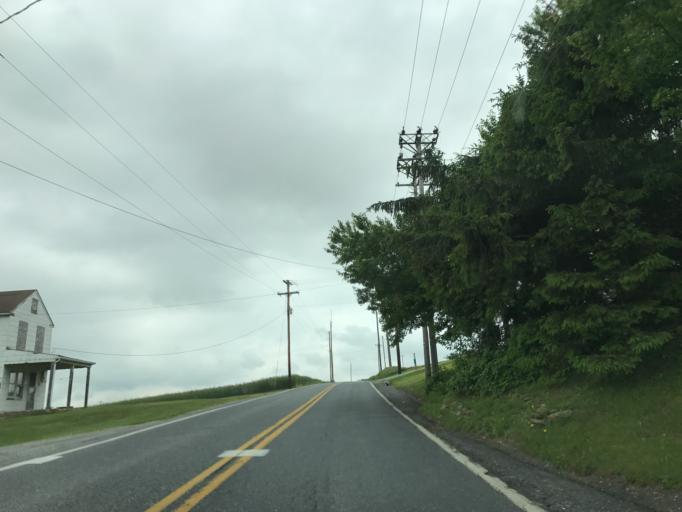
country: US
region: Pennsylvania
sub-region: York County
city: Dallastown
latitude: 39.8448
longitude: -76.6395
